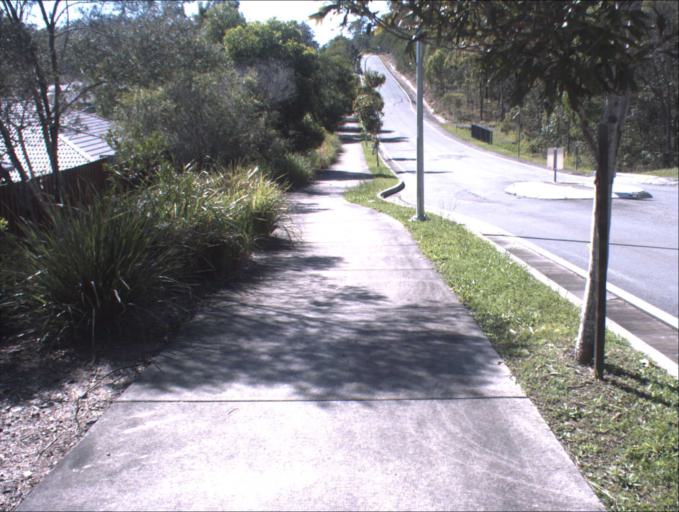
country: AU
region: Queensland
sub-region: Logan
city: Windaroo
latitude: -27.7227
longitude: 153.1702
